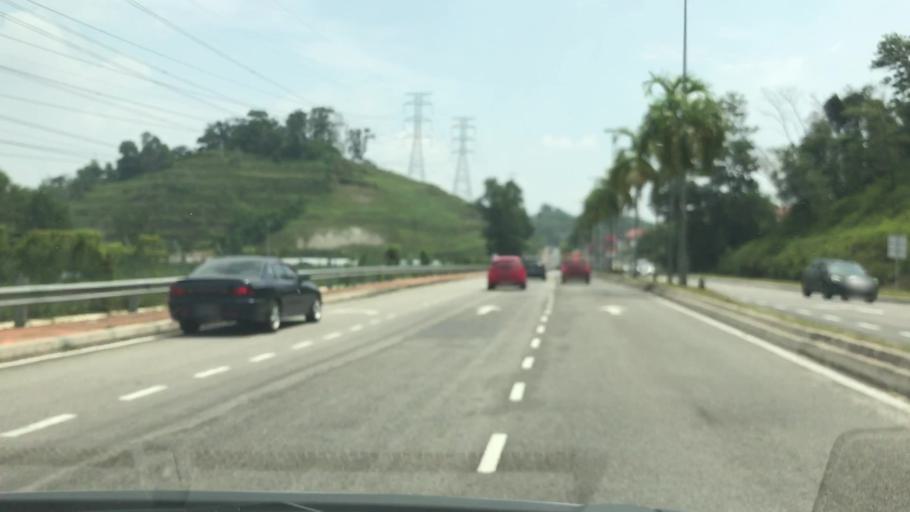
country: MY
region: Selangor
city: Kampong Baharu Balakong
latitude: 3.0347
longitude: 101.6779
